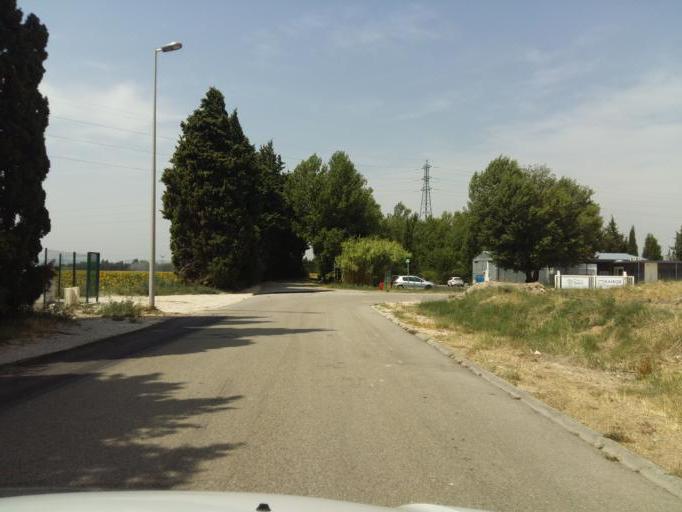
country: FR
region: Provence-Alpes-Cote d'Azur
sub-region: Departement du Vaucluse
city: Bollene
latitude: 44.3138
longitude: 4.7345
